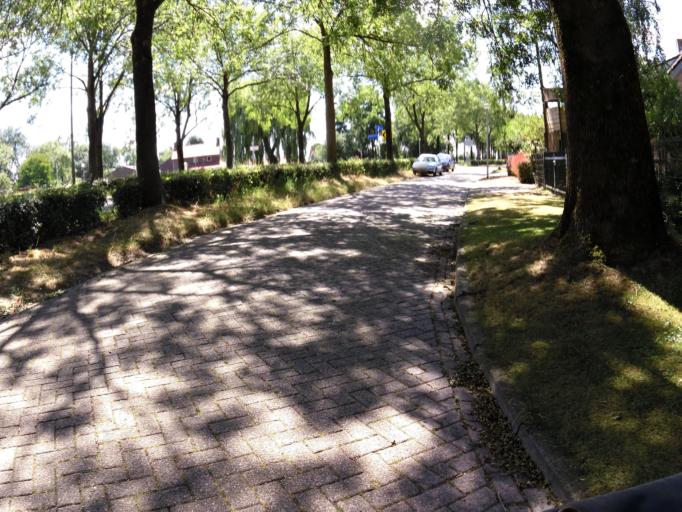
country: NL
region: Gelderland
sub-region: Gemeente Maasdriel
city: Heerewaarden
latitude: 51.7654
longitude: 5.3668
